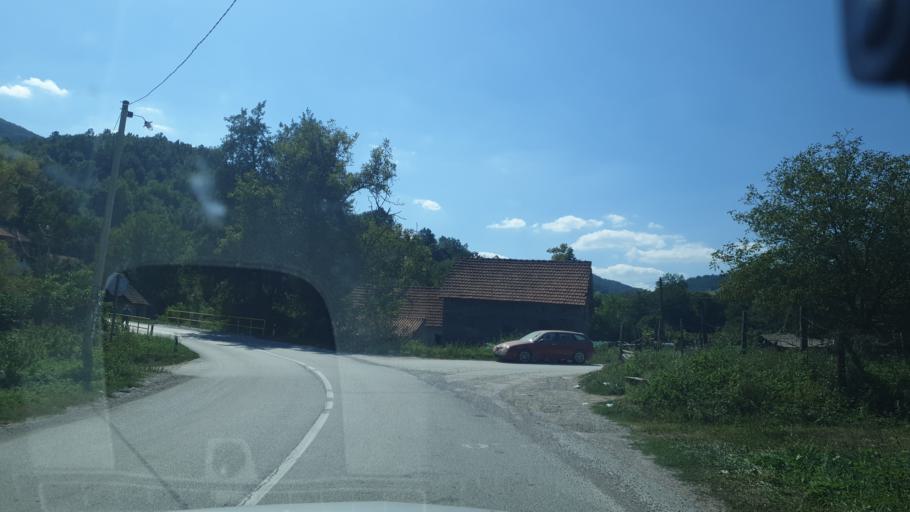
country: RS
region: Central Serbia
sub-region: Kolubarski Okrug
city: Mionica
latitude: 44.1609
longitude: 19.9847
